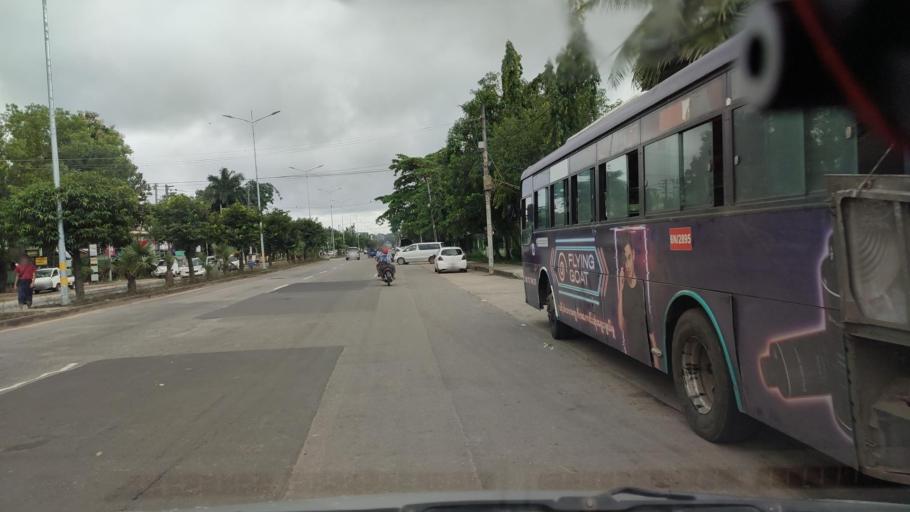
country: MM
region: Bago
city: Thanatpin
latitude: 17.0483
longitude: 96.1416
